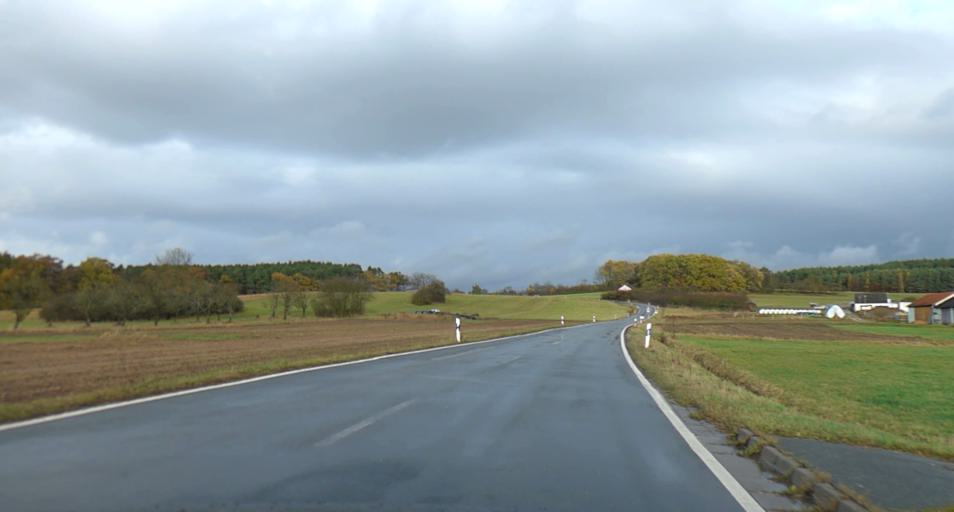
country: DE
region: Bavaria
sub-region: Upper Franconia
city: Langensendelbach
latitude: 49.6438
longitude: 11.0757
